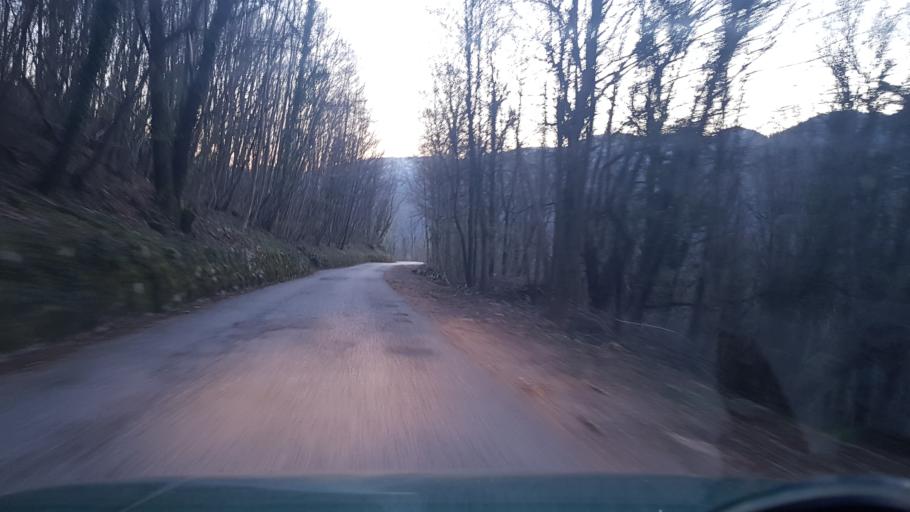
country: SI
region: Kanal
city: Kanal
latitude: 46.0789
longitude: 13.6454
